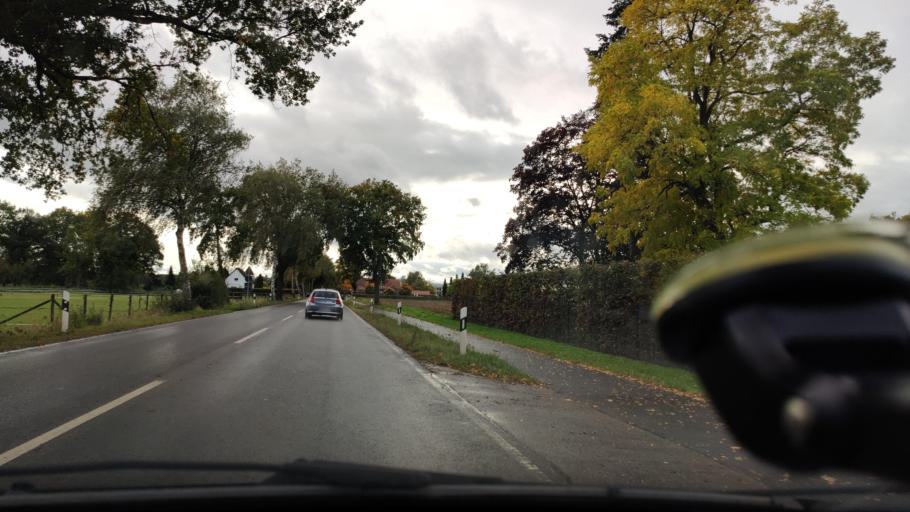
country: DE
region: North Rhine-Westphalia
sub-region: Regierungsbezirk Koln
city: Heinsberg
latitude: 51.0787
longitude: 6.1007
